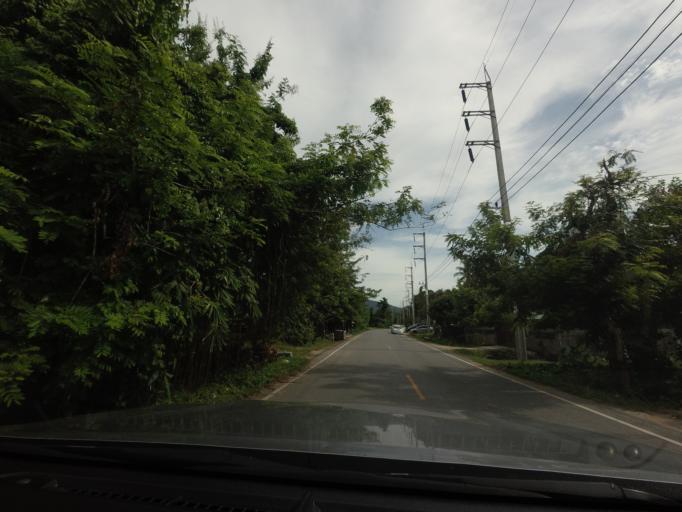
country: TH
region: Yala
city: Yala
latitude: 6.5150
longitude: 101.2893
